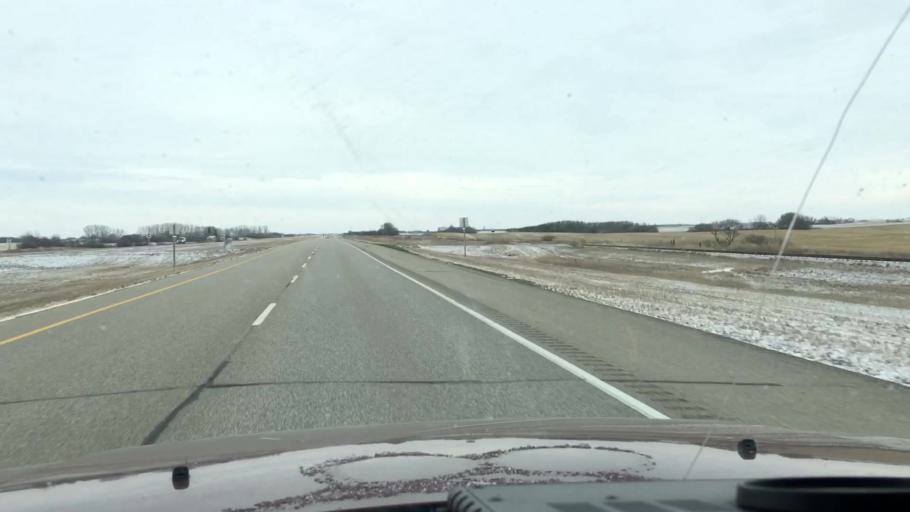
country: CA
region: Saskatchewan
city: Watrous
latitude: 51.3481
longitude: -106.1125
